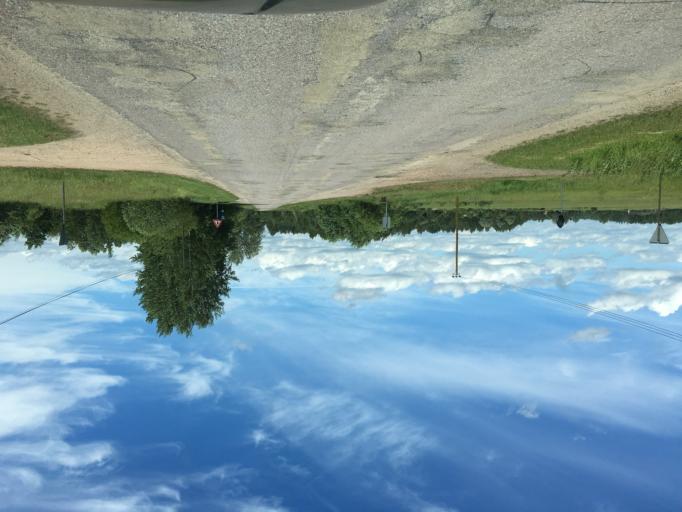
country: LV
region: Balvu Rajons
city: Balvi
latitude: 57.1564
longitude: 27.3167
